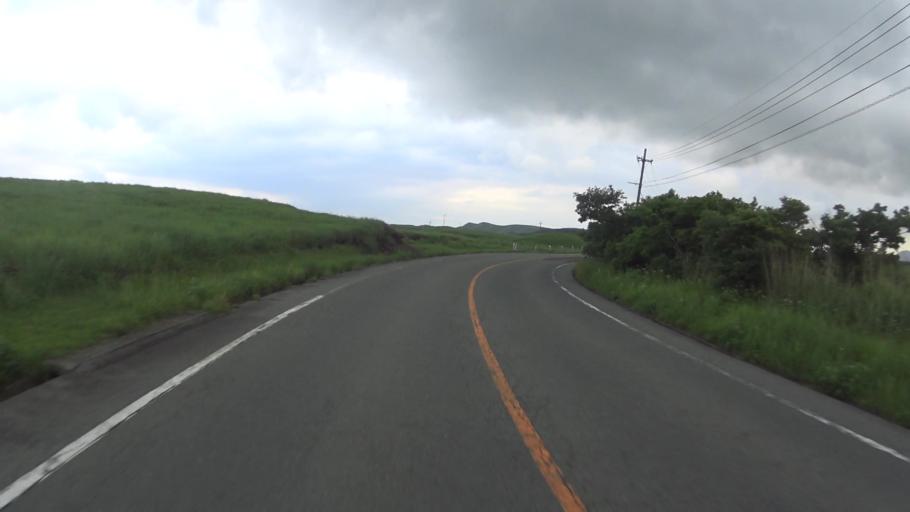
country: JP
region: Kumamoto
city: Aso
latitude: 32.9689
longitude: 131.0030
